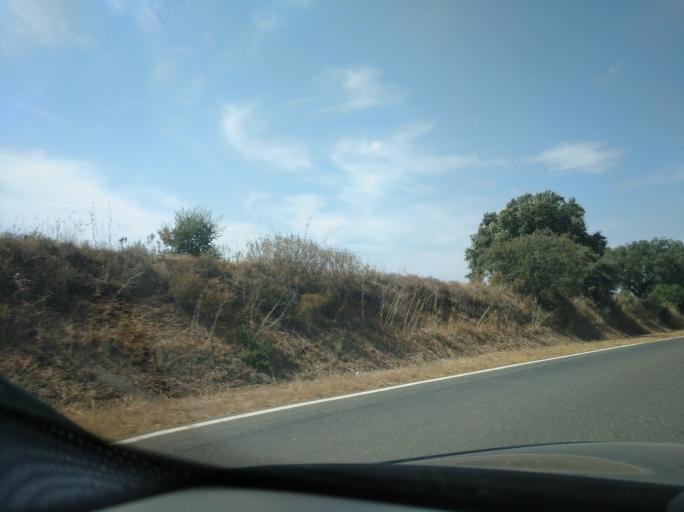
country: PT
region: Beja
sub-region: Beja
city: Beja
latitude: 37.8775
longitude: -7.8686
